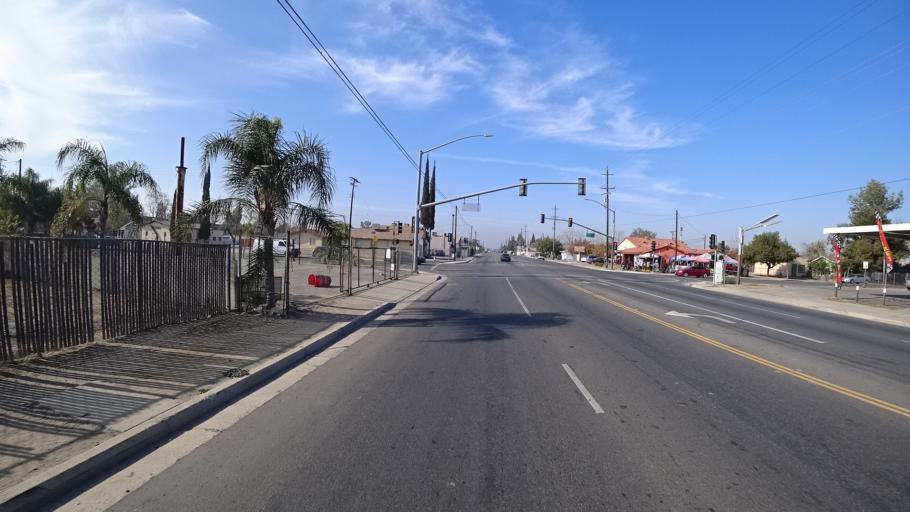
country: US
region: California
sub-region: Kern County
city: Bakersfield
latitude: 35.3539
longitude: -118.9937
